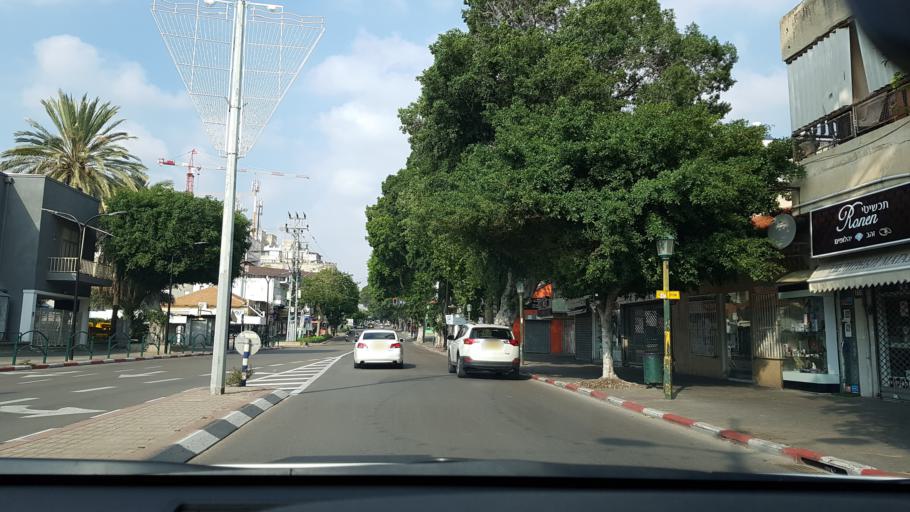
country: IL
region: Central District
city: Ness Ziona
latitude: 31.8945
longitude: 34.8116
